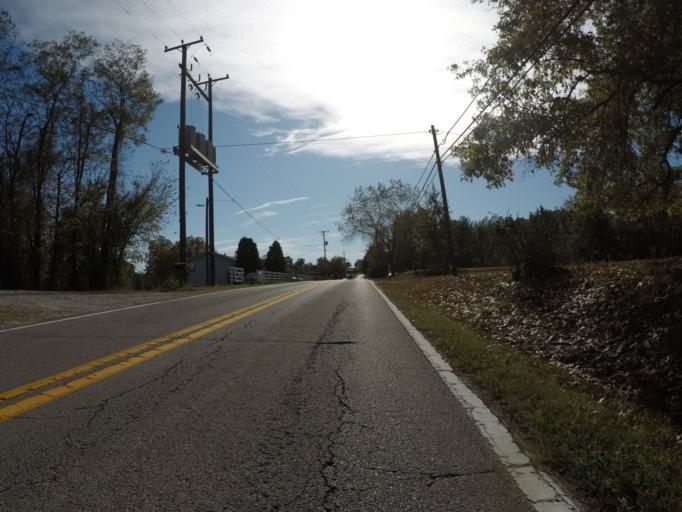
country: US
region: West Virginia
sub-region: Wayne County
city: Ceredo
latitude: 38.3610
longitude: -82.5281
